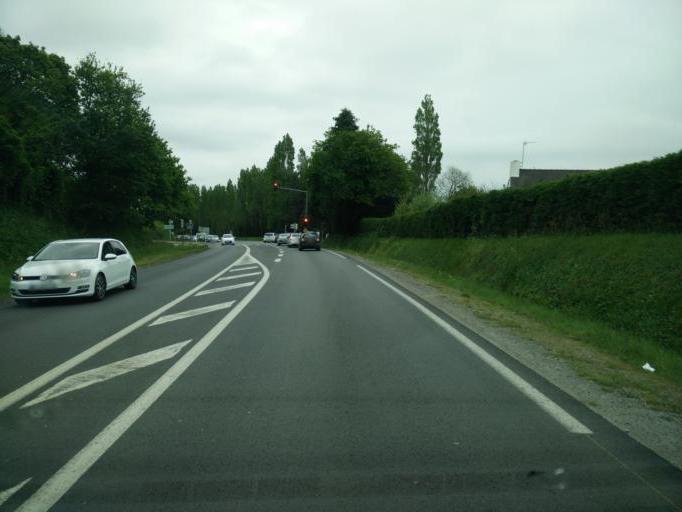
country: FR
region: Brittany
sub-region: Departement du Finistere
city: Concarneau
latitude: 47.8820
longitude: -3.9108
